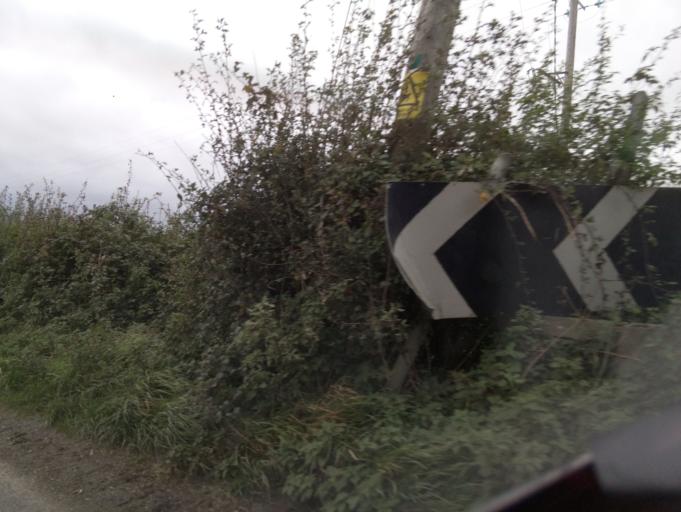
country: GB
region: England
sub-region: Somerset
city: Ilminster
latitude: 50.9552
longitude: -2.8965
